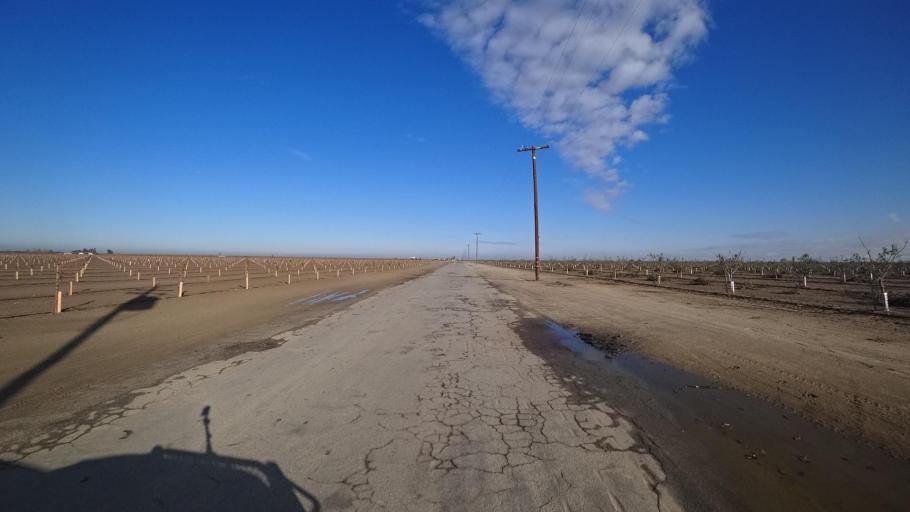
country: US
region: California
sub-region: Kern County
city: Delano
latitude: 35.7115
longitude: -119.3028
